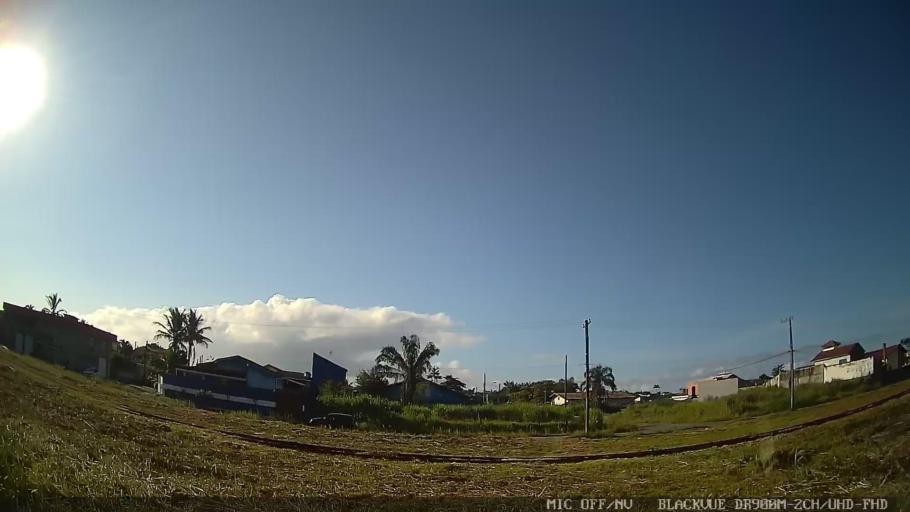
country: BR
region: Sao Paulo
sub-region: Peruibe
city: Peruibe
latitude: -24.2761
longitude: -46.9537
